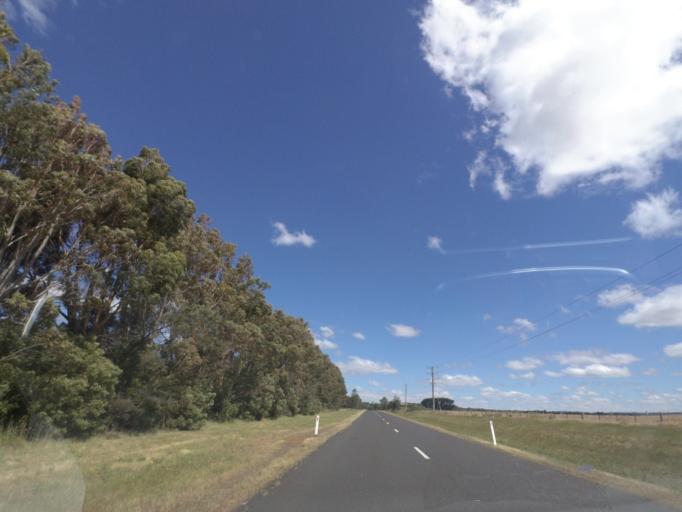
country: AU
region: Victoria
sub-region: Hume
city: Sunbury
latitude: -37.3137
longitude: 144.5191
